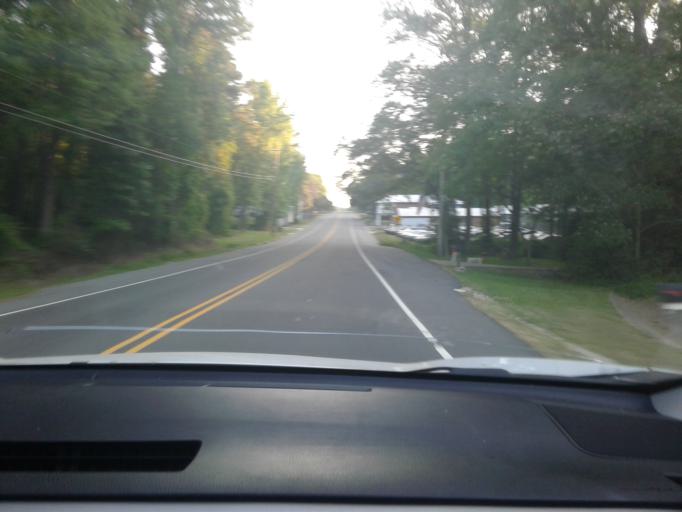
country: US
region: North Carolina
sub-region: Harnett County
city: Angier
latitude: 35.5059
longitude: -78.8136
